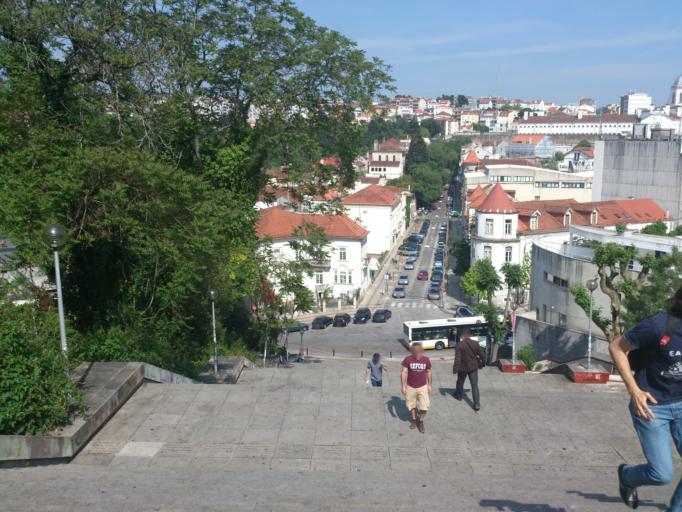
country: PT
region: Coimbra
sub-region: Coimbra
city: Coimbra
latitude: 40.2081
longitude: -8.4224
